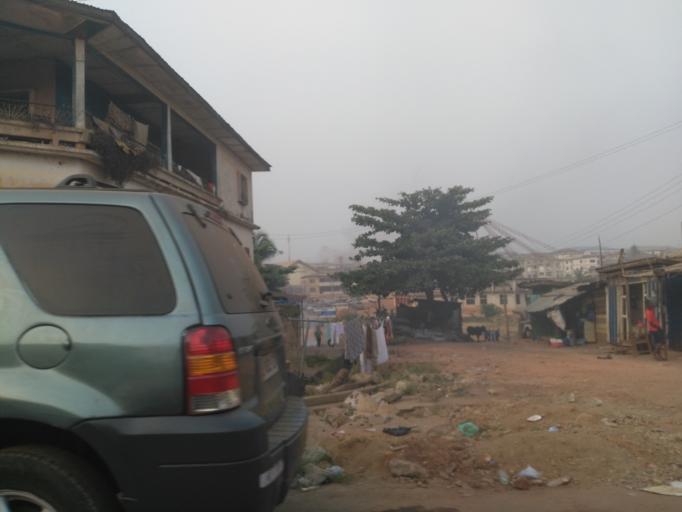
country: GH
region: Ashanti
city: Kumasi
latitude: 6.7085
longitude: -1.6184
